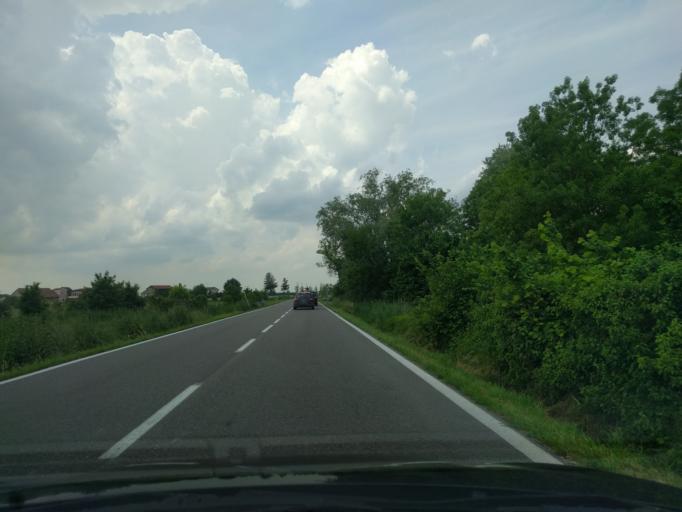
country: IT
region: Veneto
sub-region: Provincia di Rovigo
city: Villanova del Ghebbo Canton
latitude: 45.0756
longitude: 11.6424
